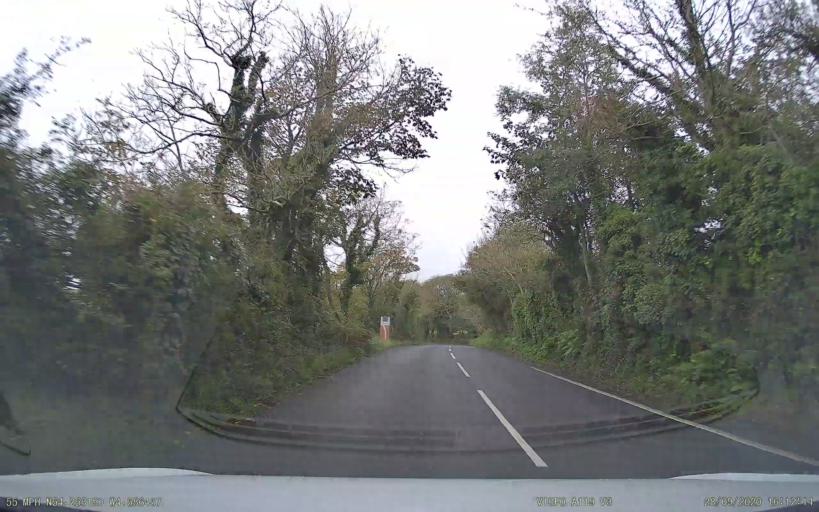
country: IM
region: Douglas
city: Douglas
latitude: 54.2532
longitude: -4.5865
